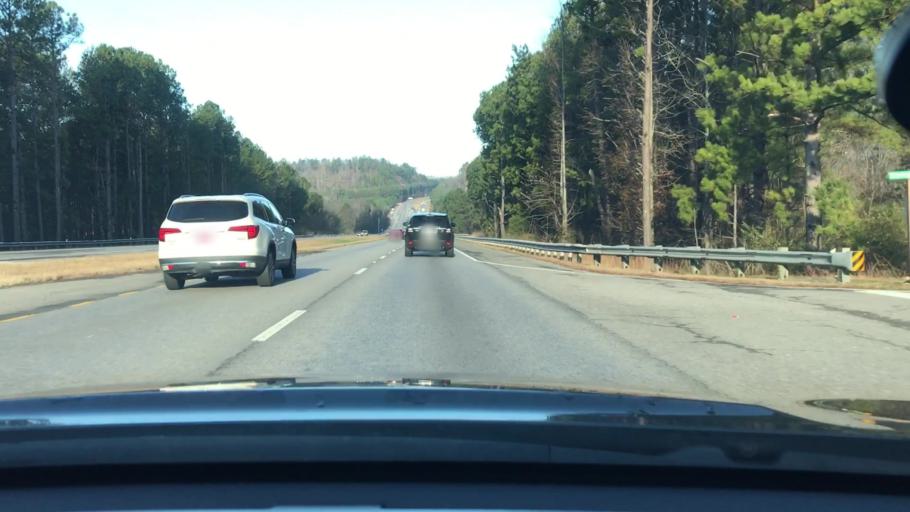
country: US
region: Alabama
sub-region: Shelby County
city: Chelsea
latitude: 33.3509
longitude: -86.6437
